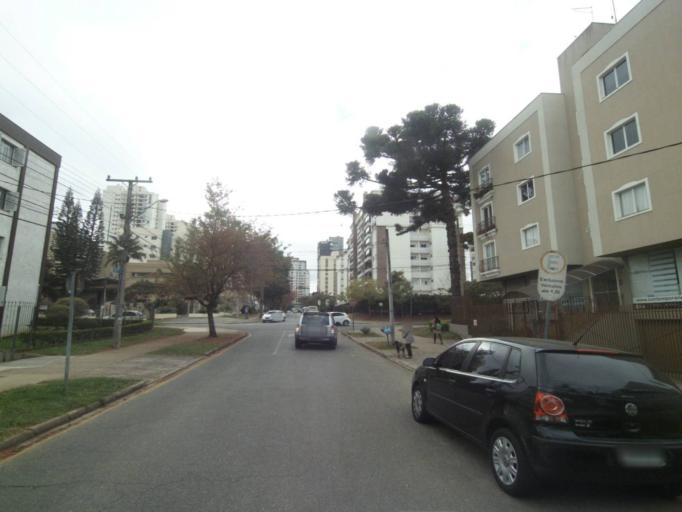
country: BR
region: Parana
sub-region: Curitiba
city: Curitiba
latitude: -25.4558
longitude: -49.2920
